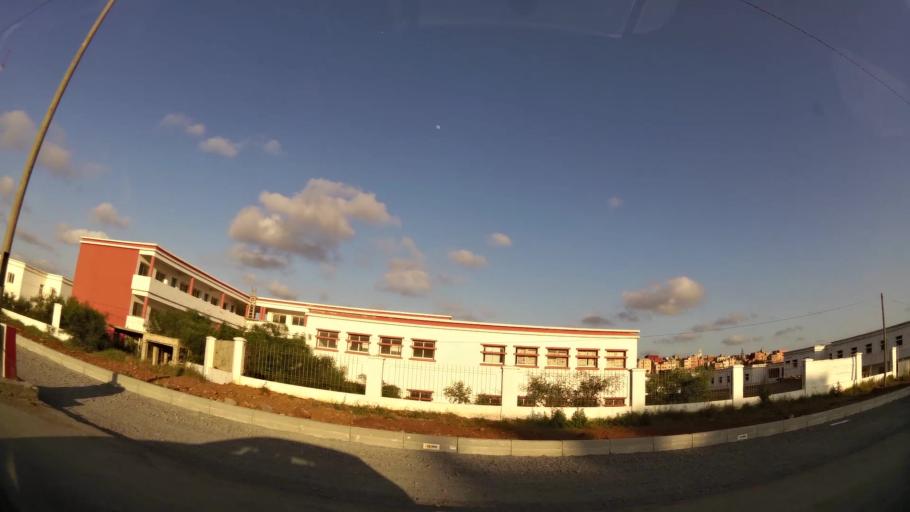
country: MA
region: Rabat-Sale-Zemmour-Zaer
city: Sale
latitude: 34.1273
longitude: -6.7356
